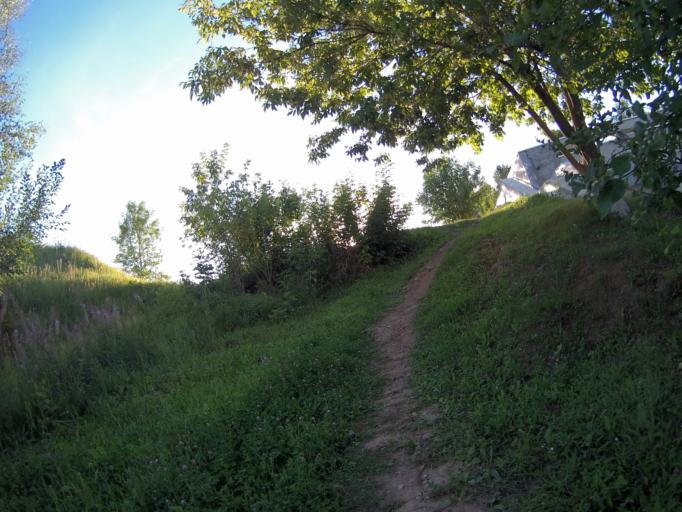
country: RU
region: Vladimir
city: Vladimir
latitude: 56.1447
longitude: 40.3732
